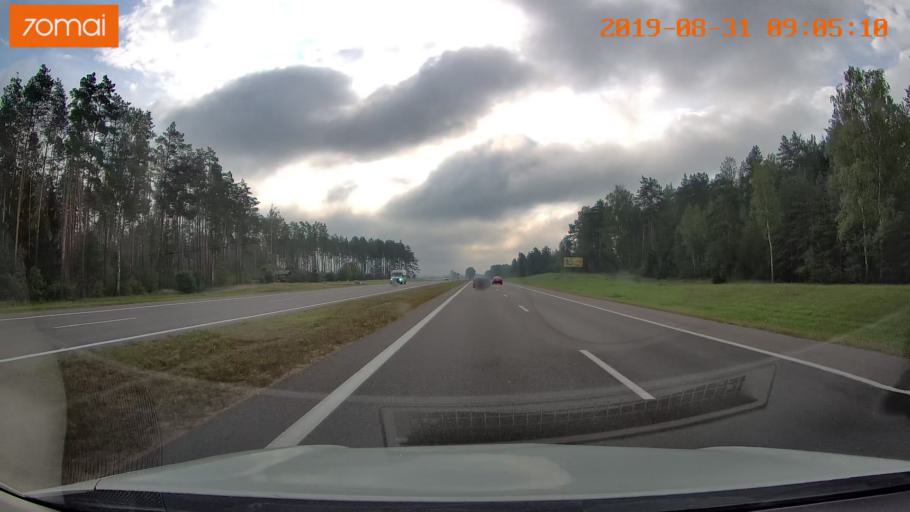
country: BY
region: Minsk
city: Chervyen'
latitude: 53.7273
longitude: 28.3676
